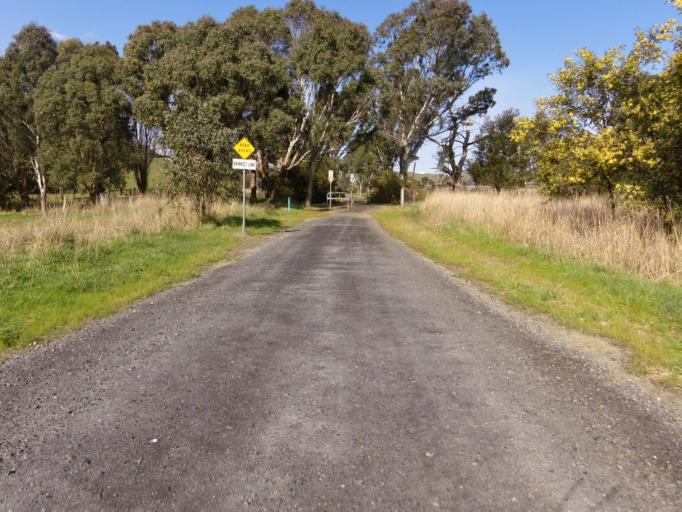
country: AU
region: Victoria
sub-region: Murrindindi
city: Alexandra
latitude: -37.0179
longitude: 145.7992
